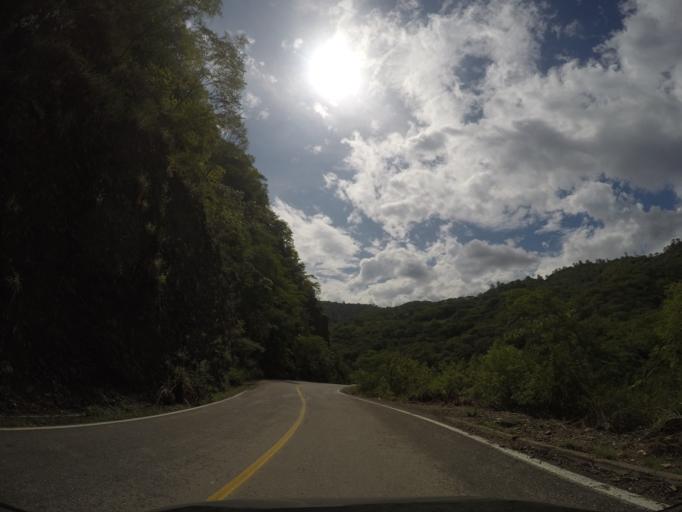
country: MX
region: Oaxaca
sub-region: San Jeronimo Coatlan
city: San Cristobal Honduras
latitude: 16.3708
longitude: -97.0870
